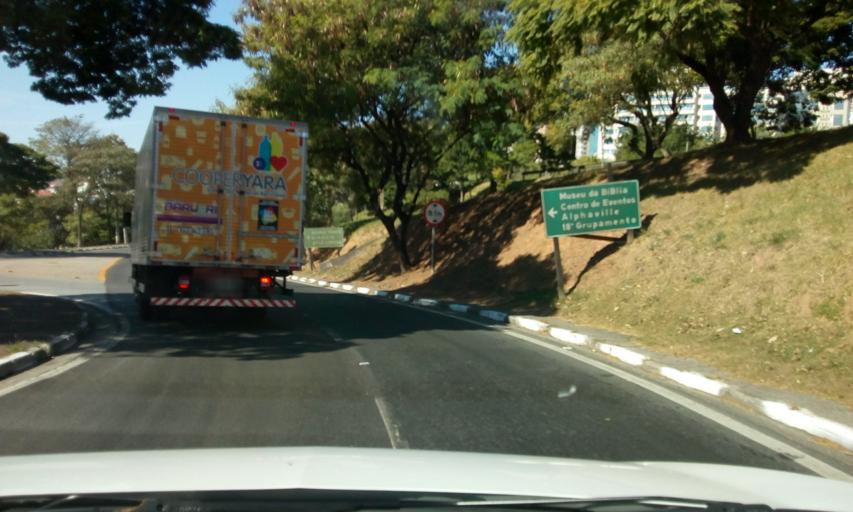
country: BR
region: Sao Paulo
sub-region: Barueri
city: Barueri
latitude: -23.5044
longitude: -46.8720
